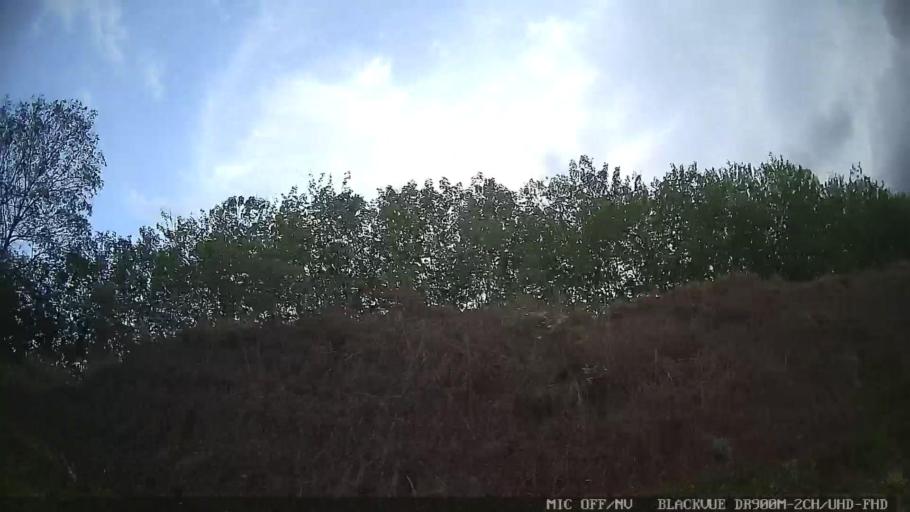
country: BR
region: Sao Paulo
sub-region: Itatiba
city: Itatiba
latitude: -22.9455
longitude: -46.8110
